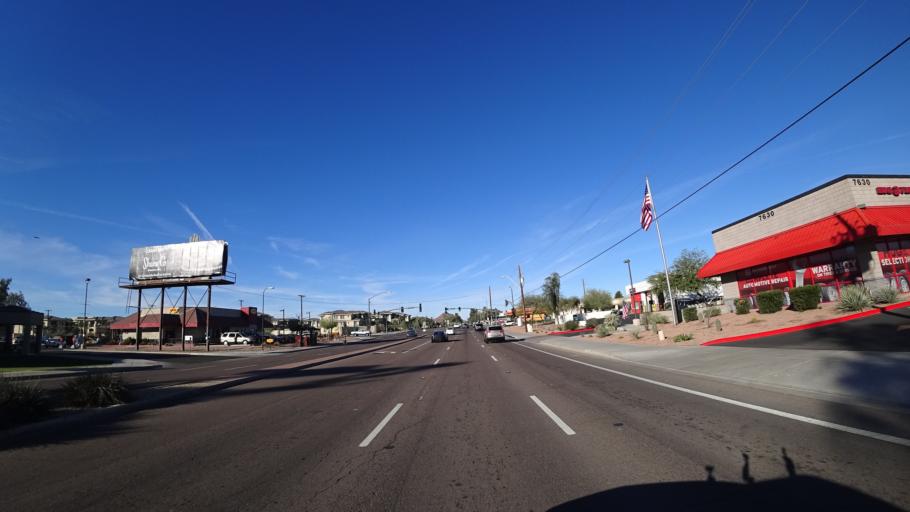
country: US
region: Arizona
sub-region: Maricopa County
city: Scottsdale
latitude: 33.4658
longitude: -111.9163
